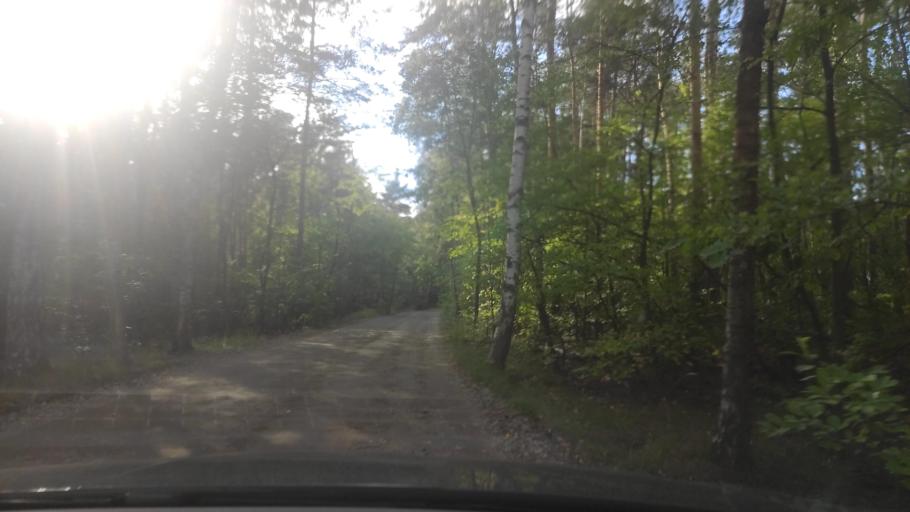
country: PL
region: Greater Poland Voivodeship
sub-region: Powiat poznanski
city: Swarzedz
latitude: 52.4160
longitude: 17.0320
